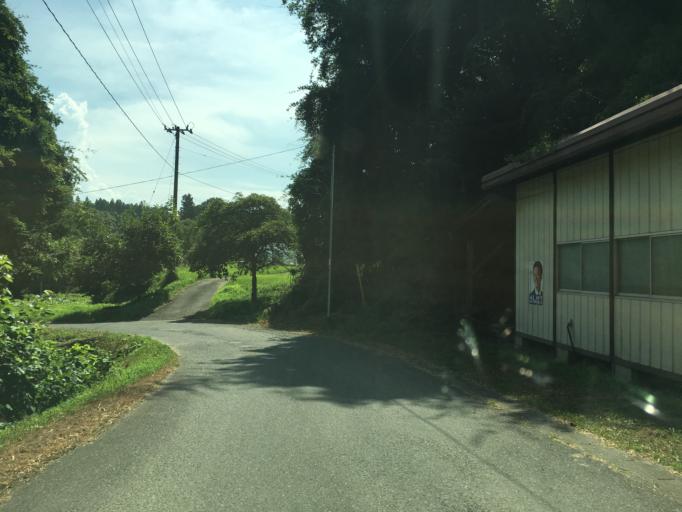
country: JP
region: Fukushima
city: Ishikawa
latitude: 37.1928
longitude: 140.4709
